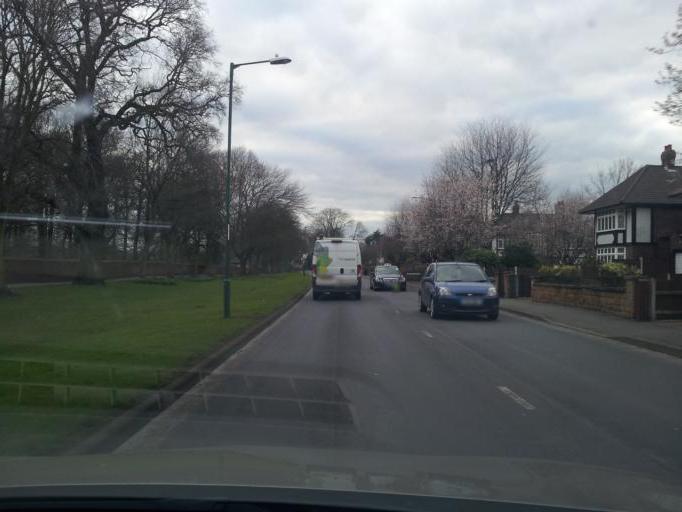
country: GB
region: England
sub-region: Nottinghamshire
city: Kimberley
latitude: 52.9534
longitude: -1.2143
